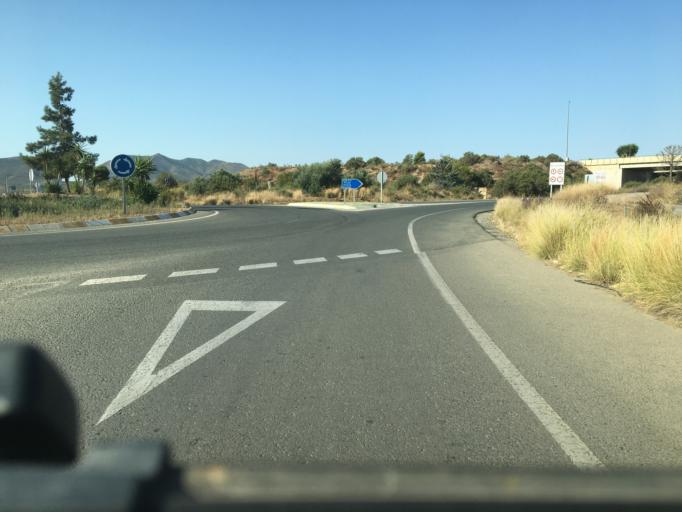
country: ES
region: Murcia
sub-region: Murcia
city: Puerto Lumbreras
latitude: 37.5393
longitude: -1.8141
